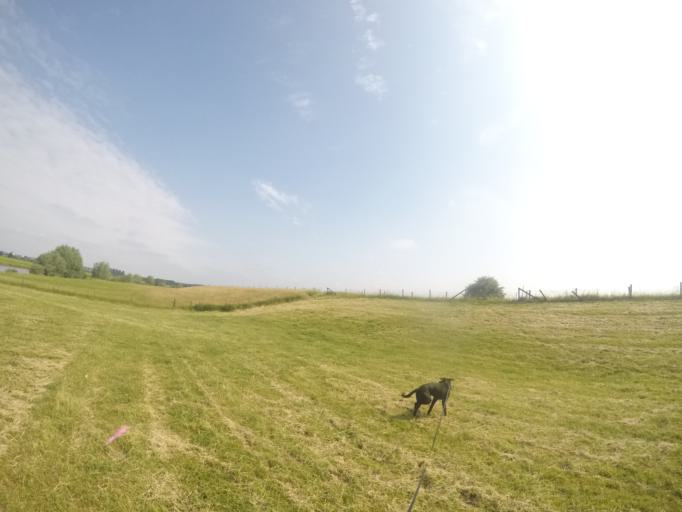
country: NL
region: Gelderland
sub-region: Gemeente Westervoort
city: Westervoort
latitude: 51.9552
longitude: 5.9509
